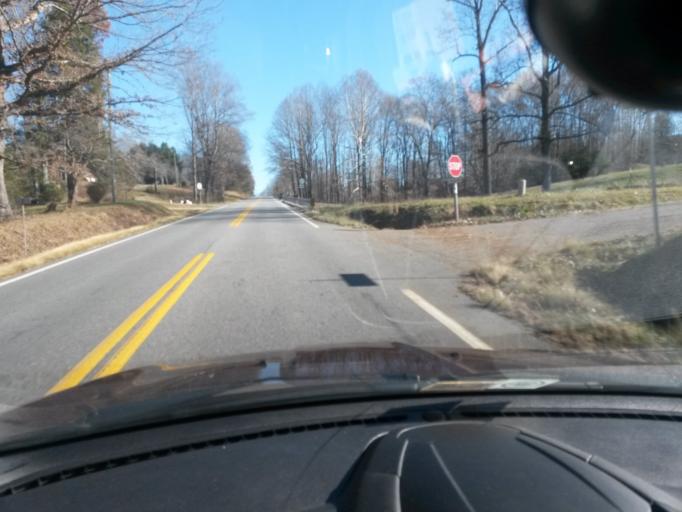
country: US
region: Virginia
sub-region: Patrick County
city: Patrick Springs
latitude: 36.7744
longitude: -80.1410
